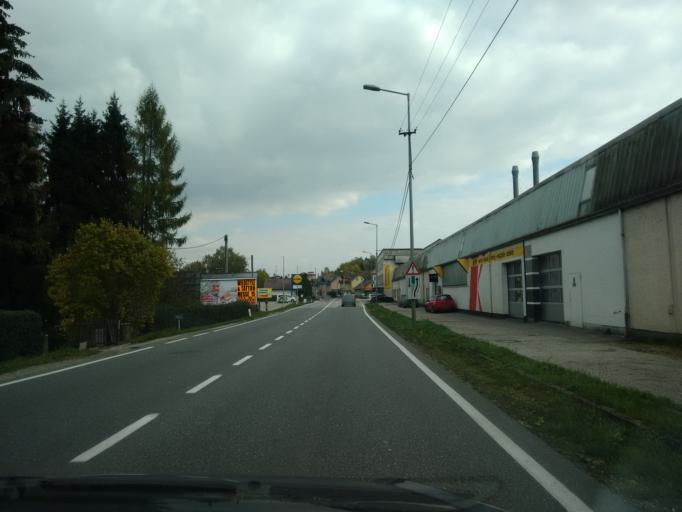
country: AT
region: Upper Austria
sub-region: Politischer Bezirk Vocklabruck
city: Attnang-Puchheim
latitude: 48.0058
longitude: 13.7051
